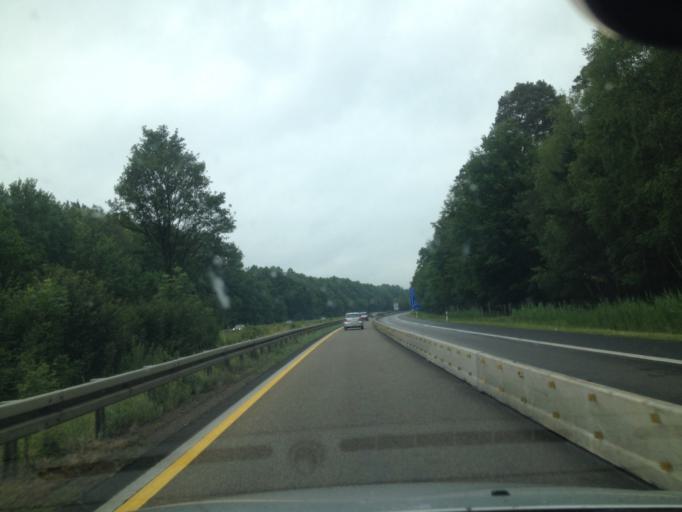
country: DE
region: Hesse
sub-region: Regierungsbezirk Darmstadt
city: Grosskrotzenburg
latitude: 50.1168
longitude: 8.9836
